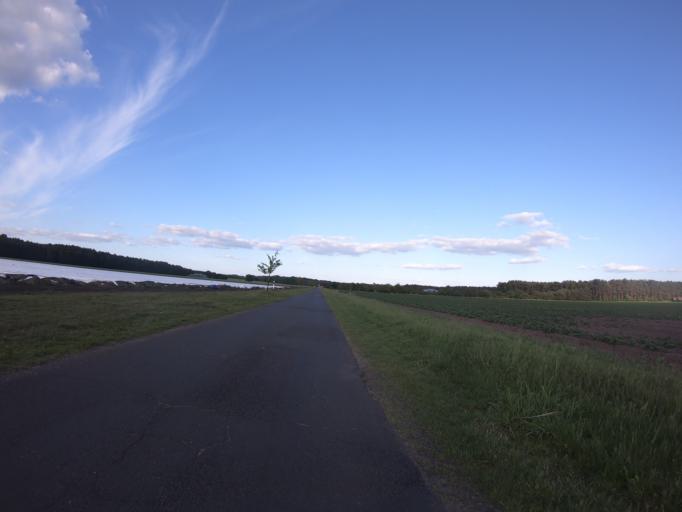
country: DE
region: Lower Saxony
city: Wagenhoff
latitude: 52.4942
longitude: 10.4899
